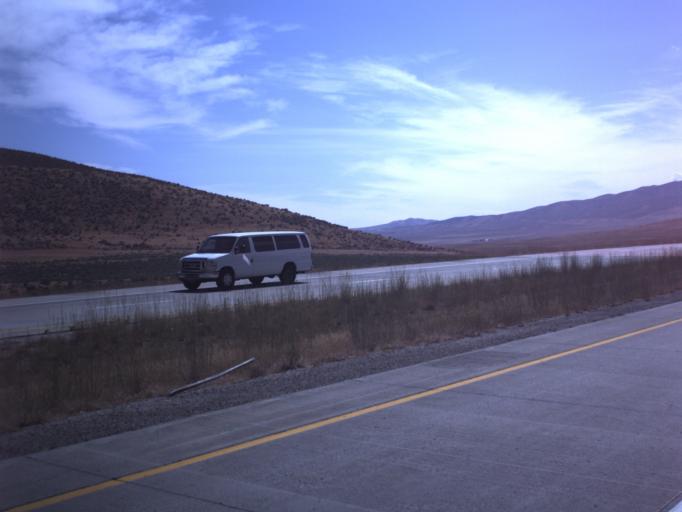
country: US
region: Utah
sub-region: Box Elder County
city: Garland
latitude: 41.8150
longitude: -112.3985
